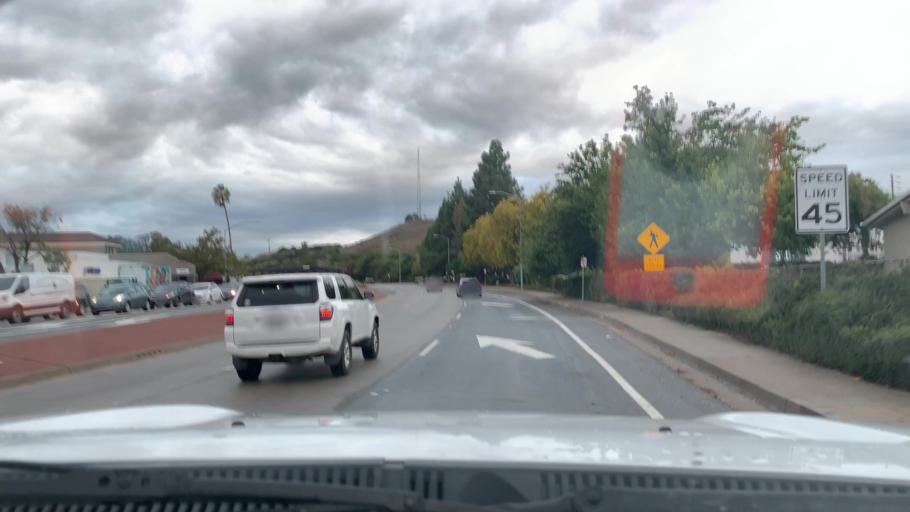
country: US
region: California
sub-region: San Luis Obispo County
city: San Luis Obispo
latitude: 35.2945
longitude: -120.6681
